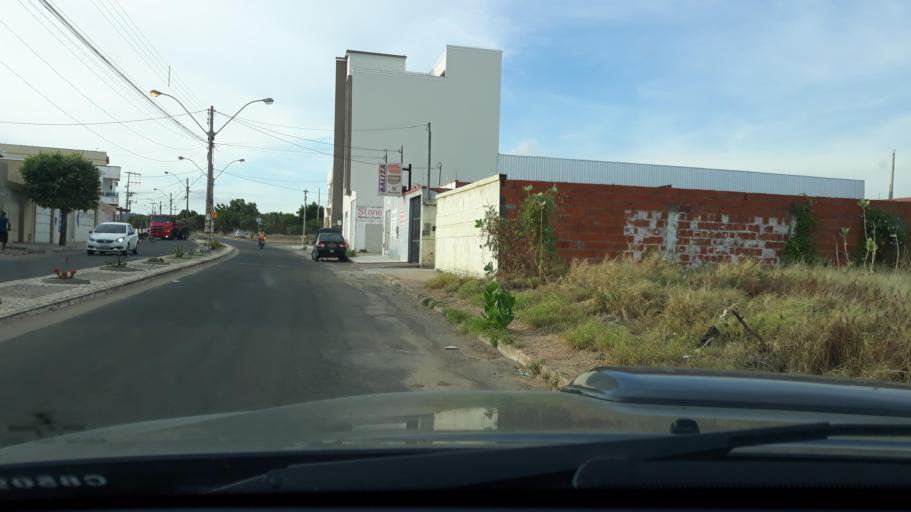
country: BR
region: Bahia
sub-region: Guanambi
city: Guanambi
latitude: -14.2323
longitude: -42.7767
